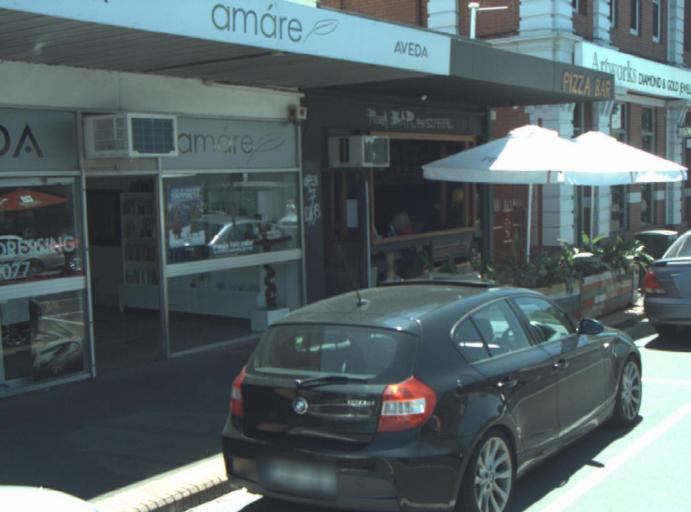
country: AU
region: Victoria
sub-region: Greater Geelong
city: Geelong West
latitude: -38.1402
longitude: 144.3484
